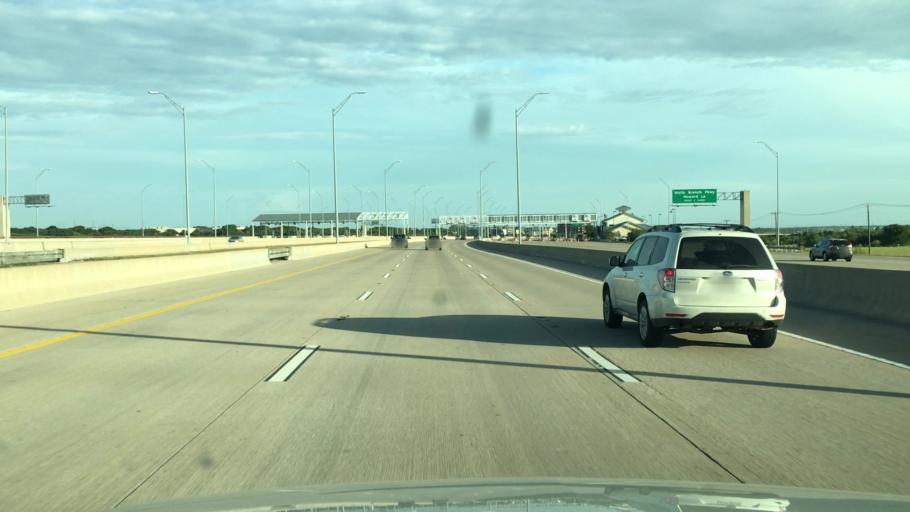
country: US
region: Texas
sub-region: Travis County
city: Wells Branch
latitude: 30.4559
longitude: -97.6979
